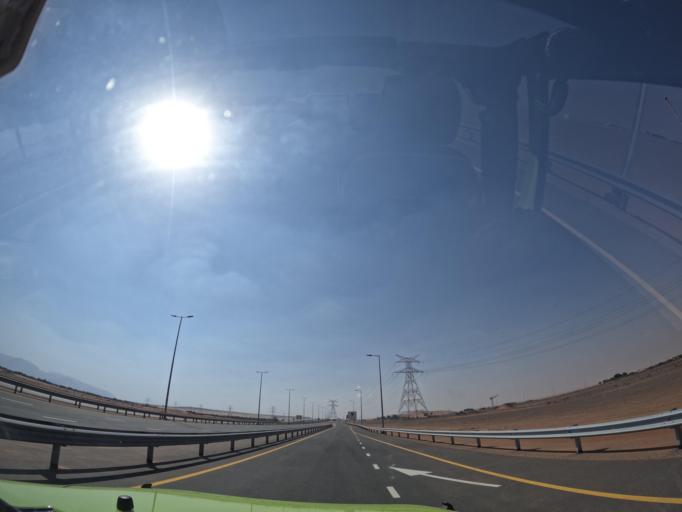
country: AE
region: Ash Shariqah
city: Adh Dhayd
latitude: 24.8098
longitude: 55.8014
